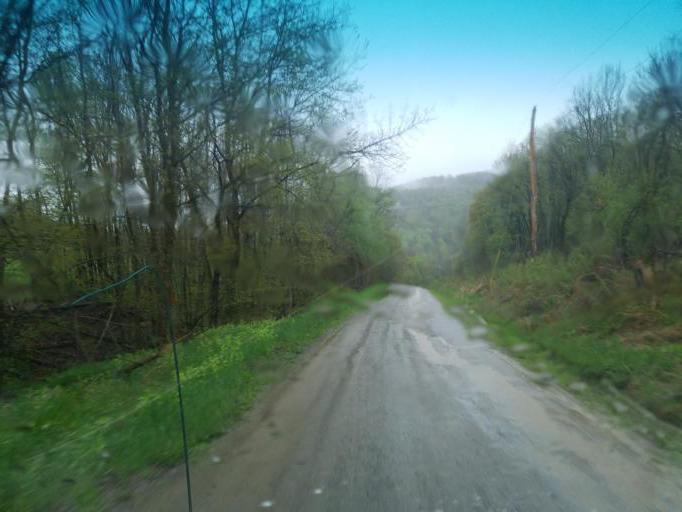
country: US
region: Pennsylvania
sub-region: Tioga County
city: Westfield
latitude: 41.9135
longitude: -77.6397
